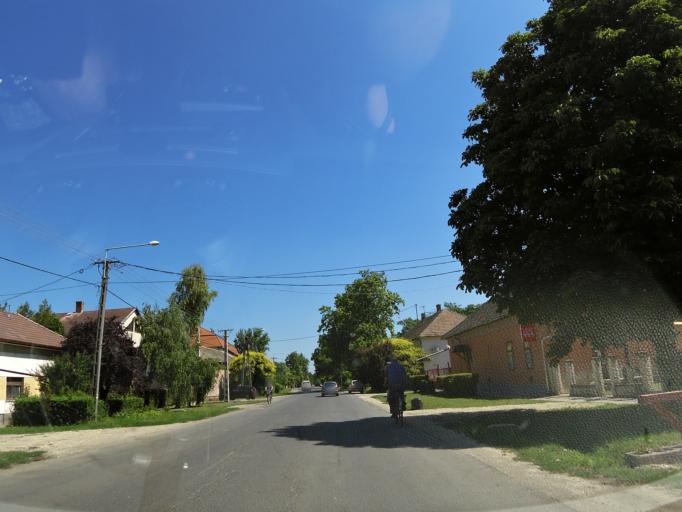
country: HU
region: Jasz-Nagykun-Szolnok
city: Kunhegyes
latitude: 47.3729
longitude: 20.6325
